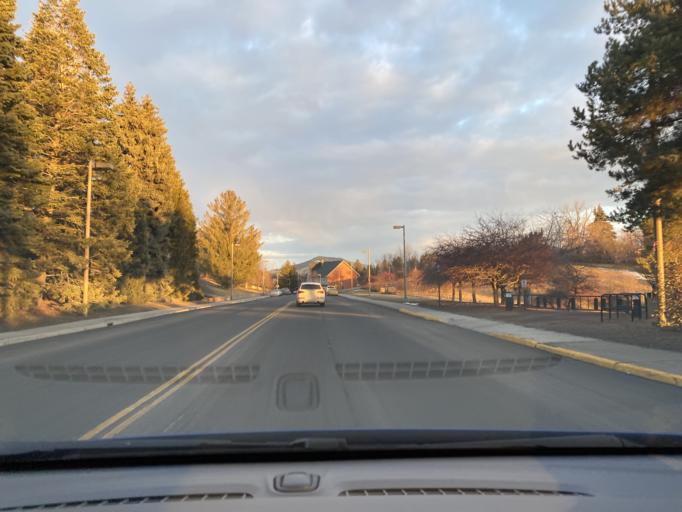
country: US
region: Idaho
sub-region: Latah County
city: Moscow
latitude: 46.7235
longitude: -117.0155
